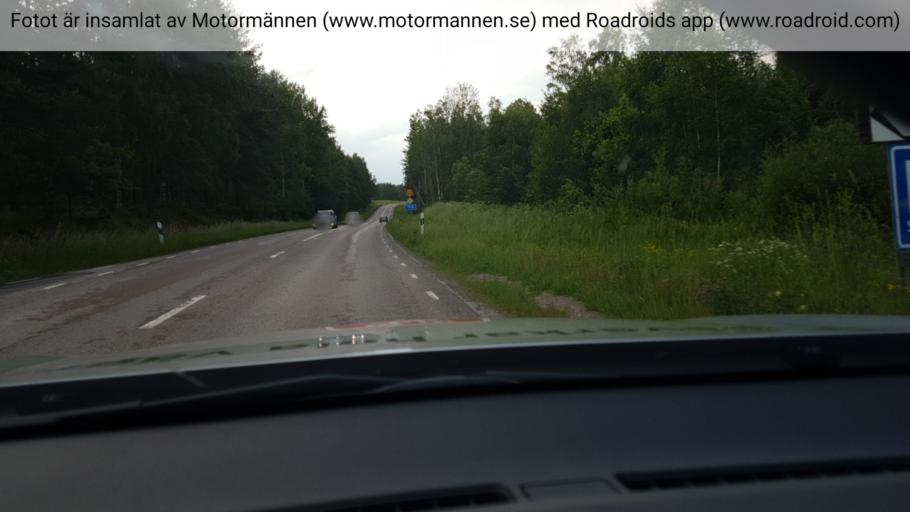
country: SE
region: Vaestra Goetaland
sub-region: Hjo Kommun
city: Hjo
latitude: 58.1830
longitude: 14.2028
